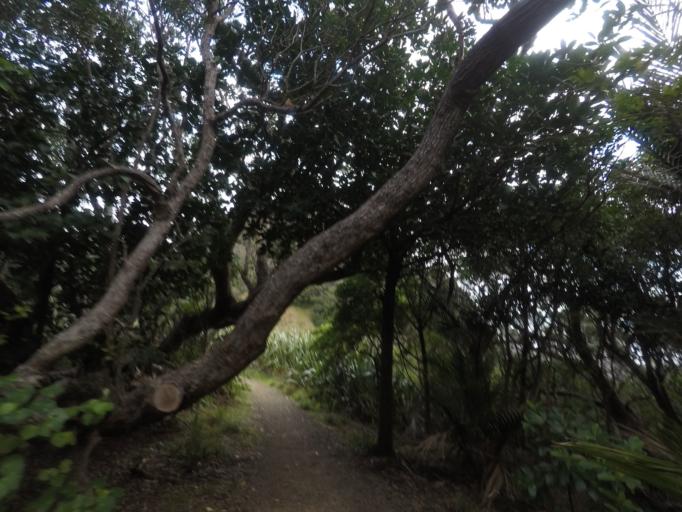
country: NZ
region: Auckland
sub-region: Auckland
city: Muriwai Beach
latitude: -36.9844
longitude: 174.4750
